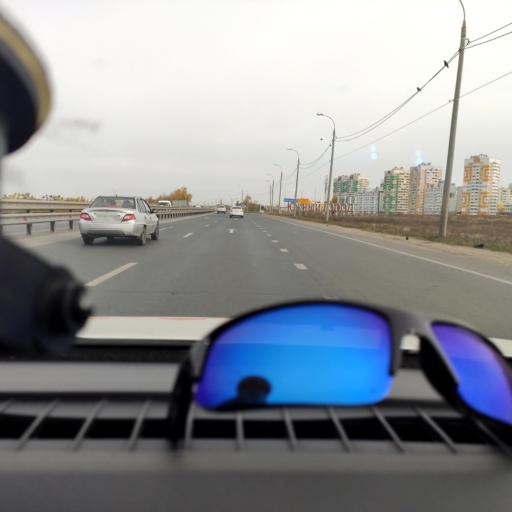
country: RU
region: Samara
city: Samara
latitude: 53.0933
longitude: 50.1533
